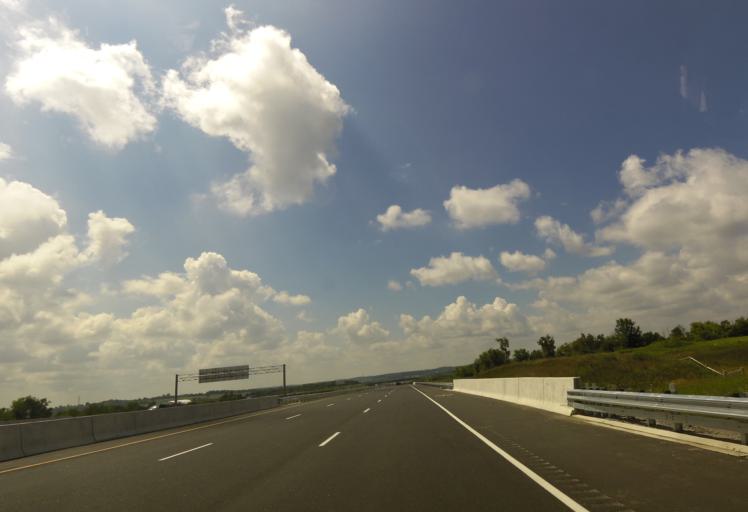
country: CA
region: Ontario
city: Ajax
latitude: 43.9453
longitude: -79.0406
